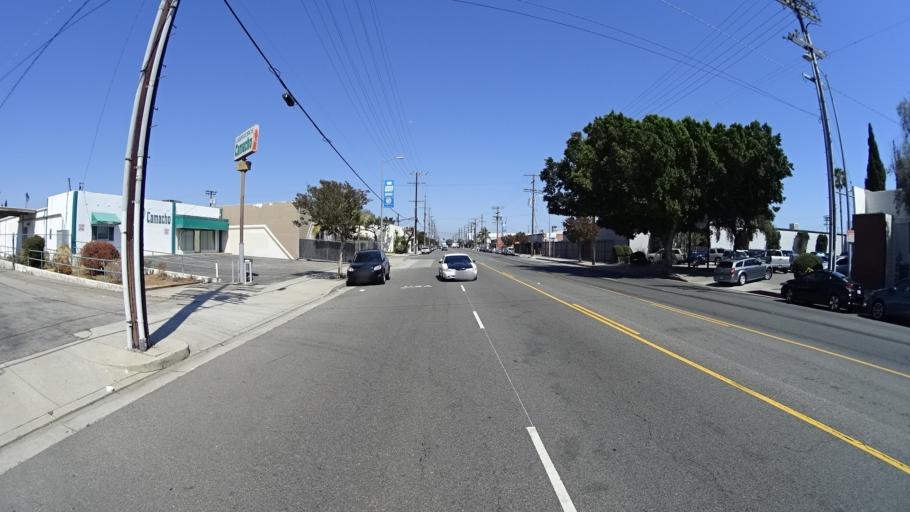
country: US
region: California
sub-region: Los Angeles County
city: Van Nuys
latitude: 34.2081
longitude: -118.4217
